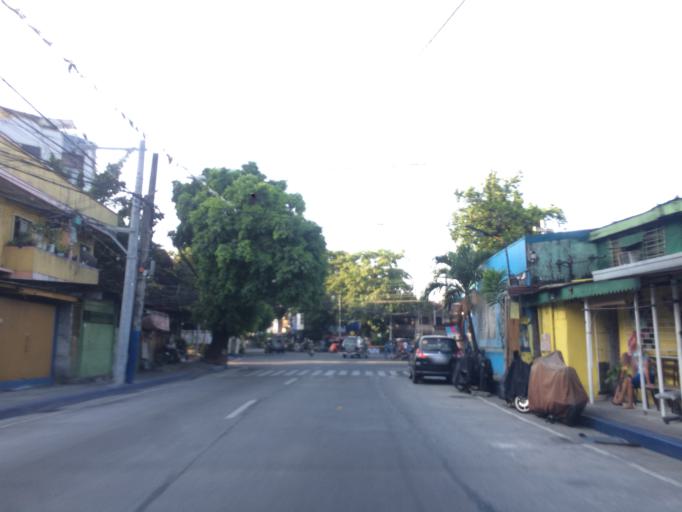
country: PH
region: Metro Manila
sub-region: City of Manila
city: Manila
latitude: 14.6176
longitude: 120.9985
